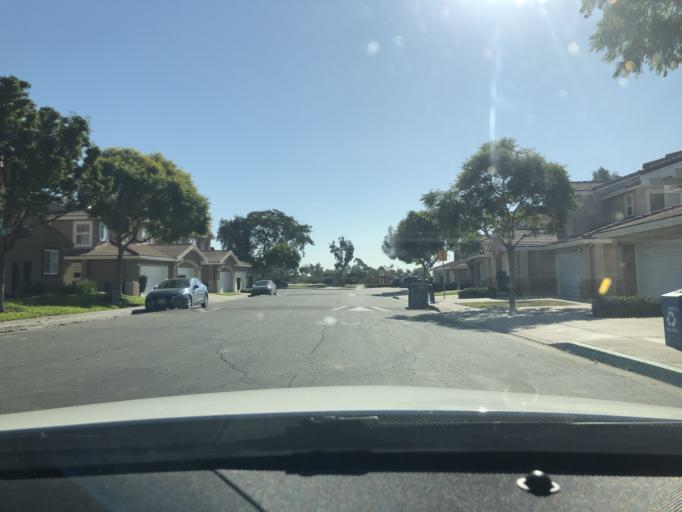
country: US
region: California
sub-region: San Diego County
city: Lemon Grove
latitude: 32.7404
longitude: -117.0663
